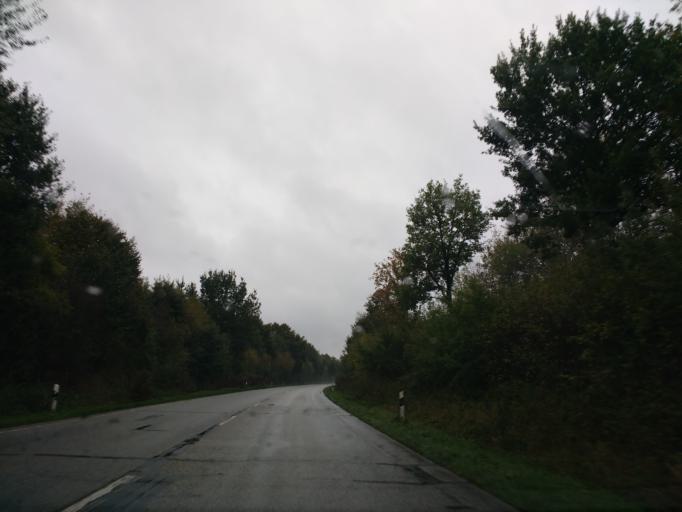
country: DE
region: Schleswig-Holstein
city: Susel
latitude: 54.0725
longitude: 10.7091
